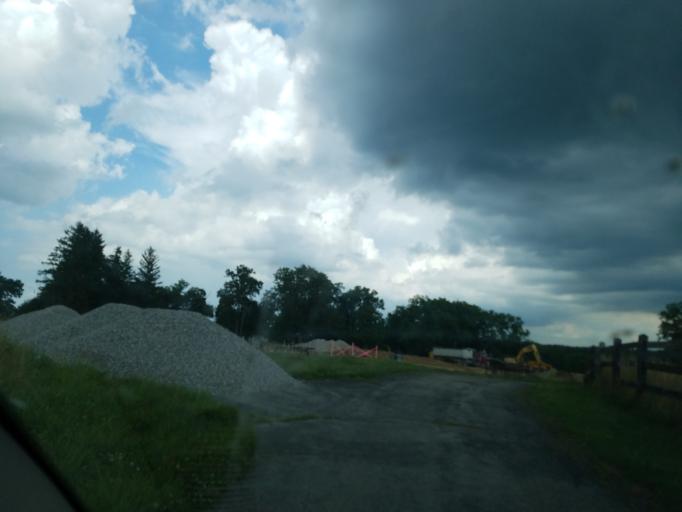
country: US
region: Ohio
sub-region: Delaware County
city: Powell
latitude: 40.1872
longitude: -83.0569
